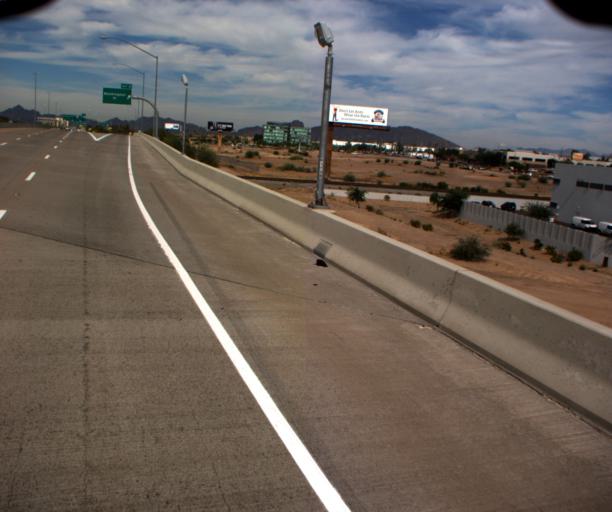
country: US
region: Arizona
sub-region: Maricopa County
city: Tempe Junction
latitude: 33.4425
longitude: -111.9802
